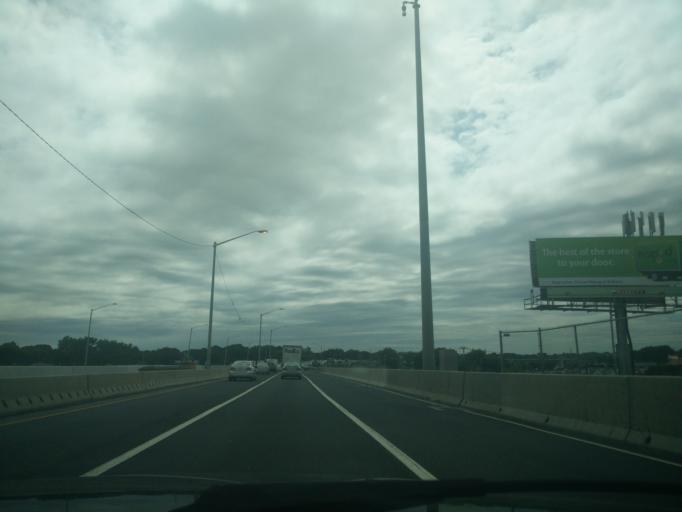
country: US
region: Connecticut
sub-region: Fairfield County
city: Stratford
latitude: 41.2016
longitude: -73.1155
